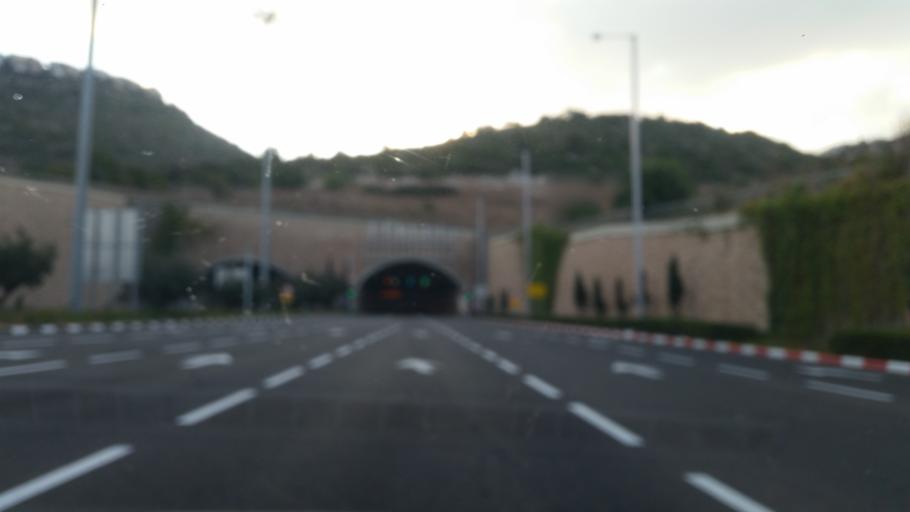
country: IL
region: Haifa
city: Tirat Karmel
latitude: 32.7922
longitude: 34.9696
